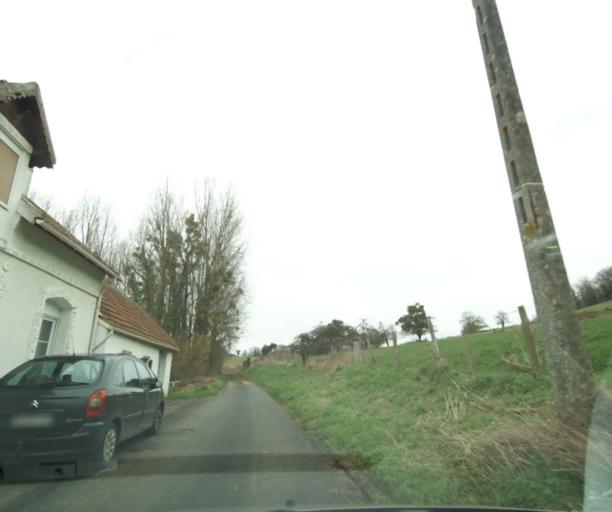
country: FR
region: Picardie
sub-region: Departement de l'Oise
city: Crisolles
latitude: 49.6025
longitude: 3.0198
